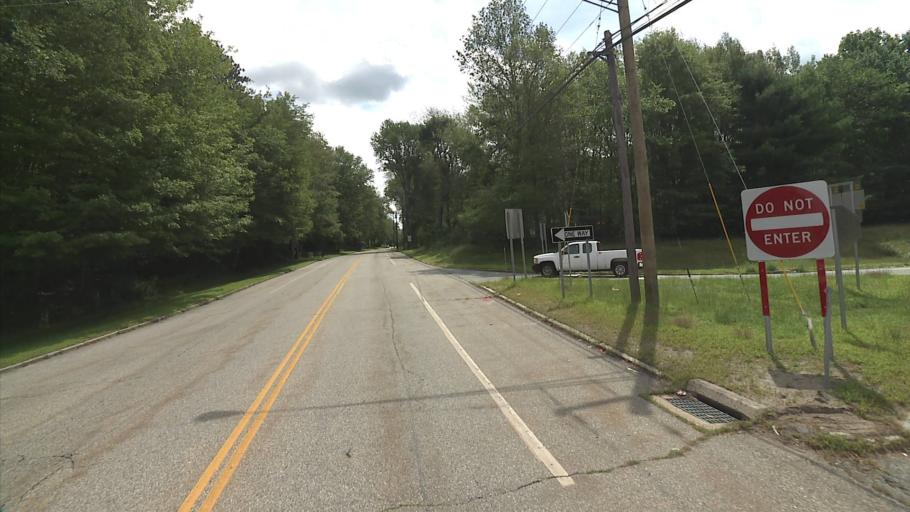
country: US
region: Connecticut
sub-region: Windham County
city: Thompson
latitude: 41.9652
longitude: -71.8715
